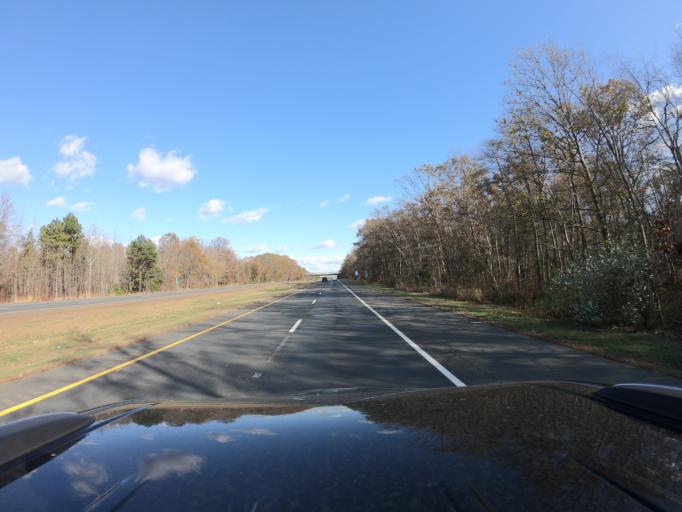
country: US
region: New Jersey
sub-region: Monmouth County
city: Farmingdale
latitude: 40.1670
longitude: -74.2022
